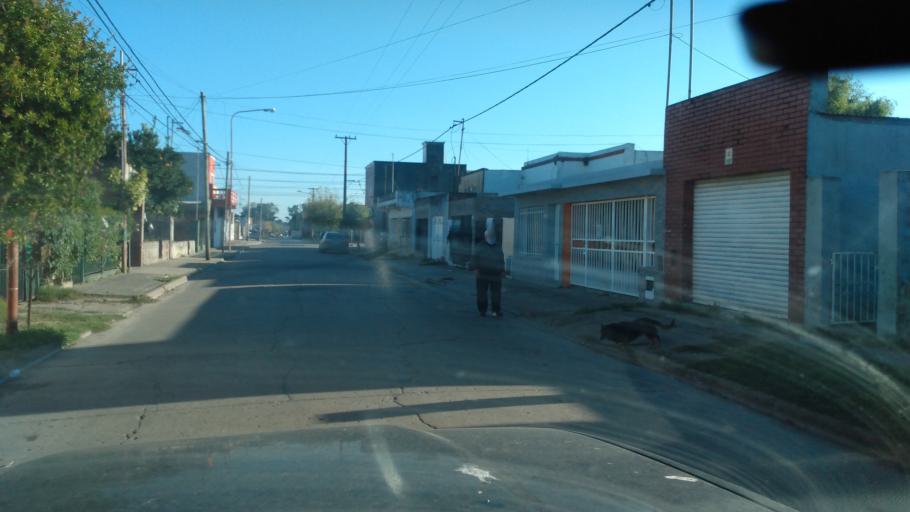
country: AR
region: Buenos Aires
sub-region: Partido de Lujan
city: Lujan
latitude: -34.5651
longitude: -59.0941
